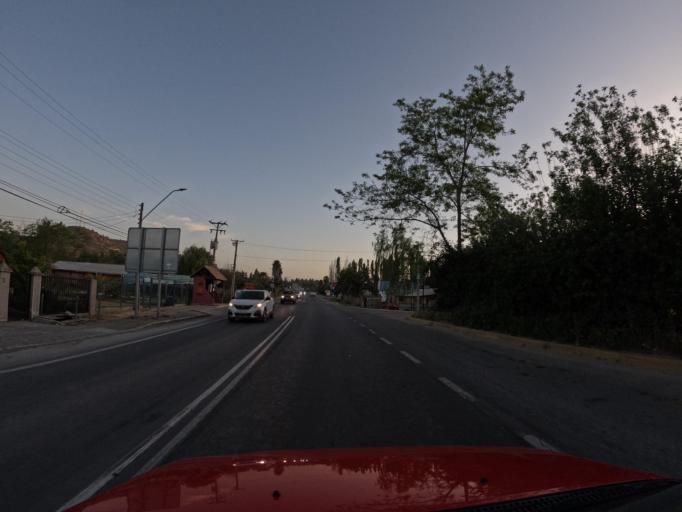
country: CL
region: O'Higgins
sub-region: Provincia de Cachapoal
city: San Vicente
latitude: -34.1678
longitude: -71.3968
